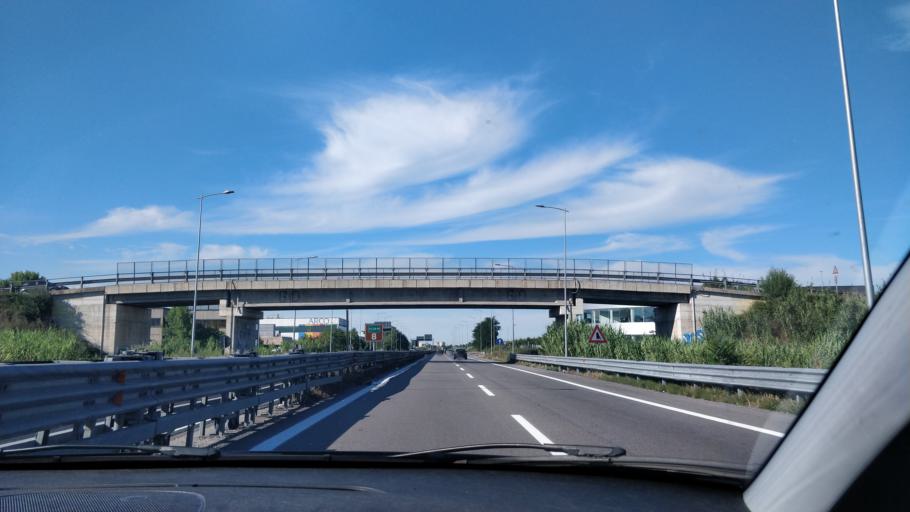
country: IT
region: Abruzzo
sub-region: Provincia di Pescara
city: Santa Teresa
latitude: 42.4172
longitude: 14.1675
